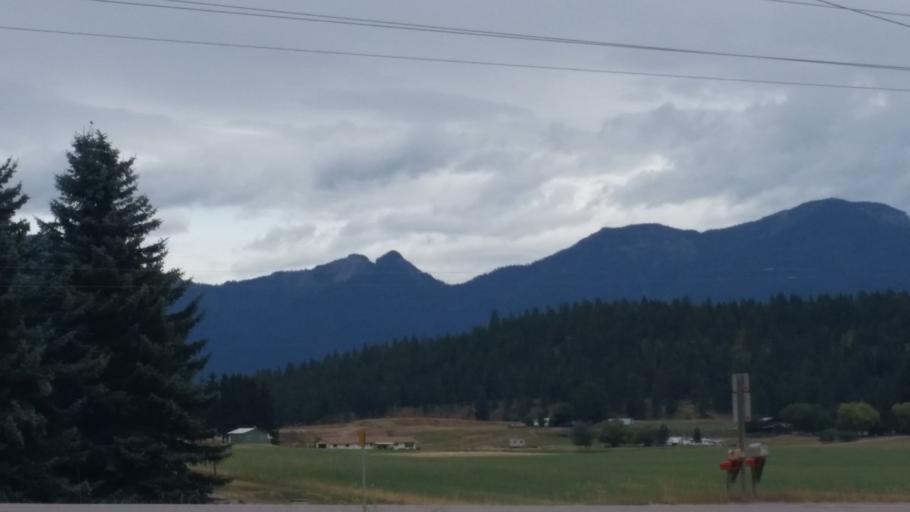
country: US
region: Montana
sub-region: Flathead County
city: Bigfork
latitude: 48.0954
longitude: -114.0882
